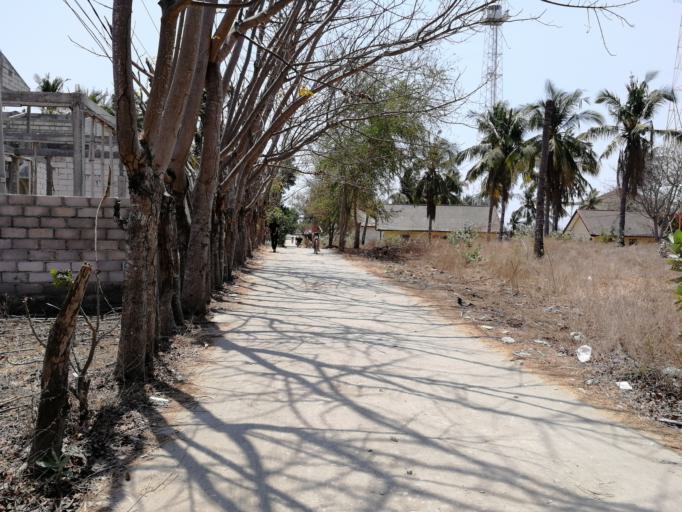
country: ID
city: Gili Trawangan
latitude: -8.3451
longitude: 116.0304
